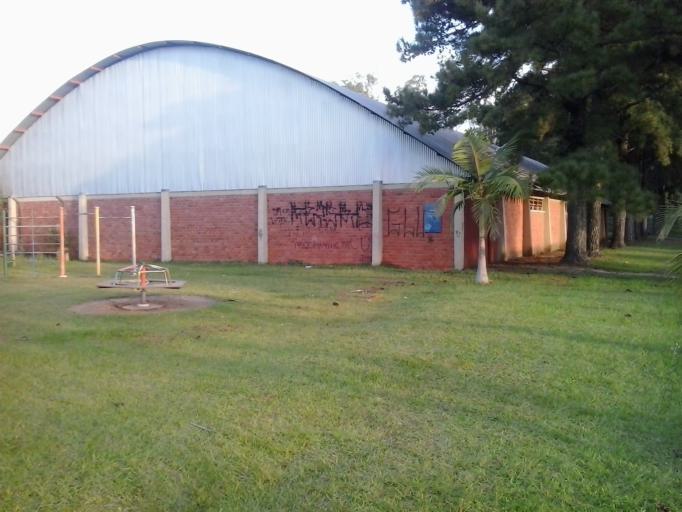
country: BR
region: Rio Grande do Sul
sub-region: Santa Maria
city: Santa Maria
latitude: -29.7209
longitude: -53.7102
